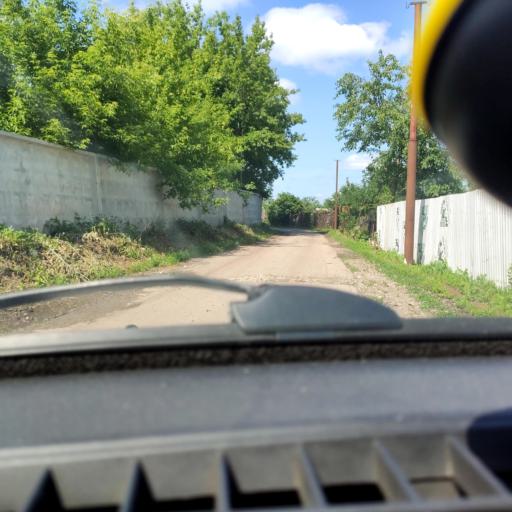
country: RU
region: Samara
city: Tol'yatti
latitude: 53.5583
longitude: 49.4473
